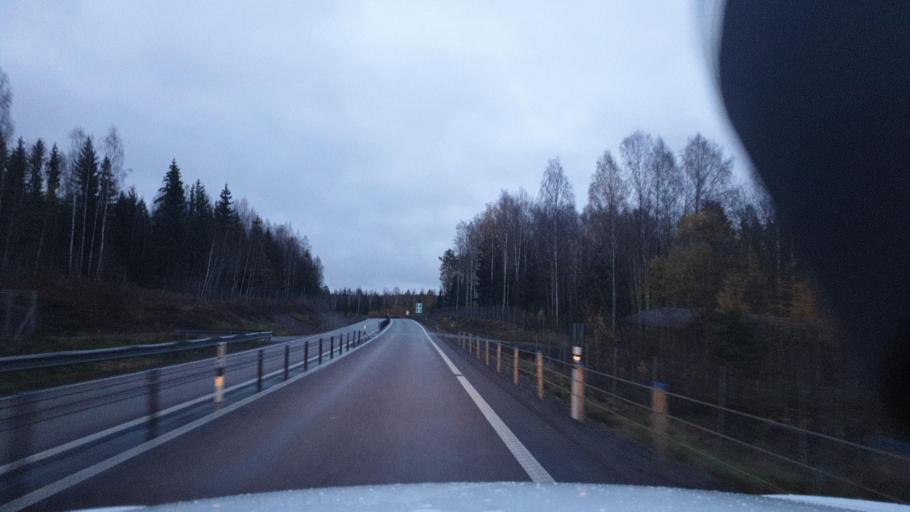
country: SE
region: Vaermland
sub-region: Eda Kommun
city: Amotfors
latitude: 59.7564
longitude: 12.4288
